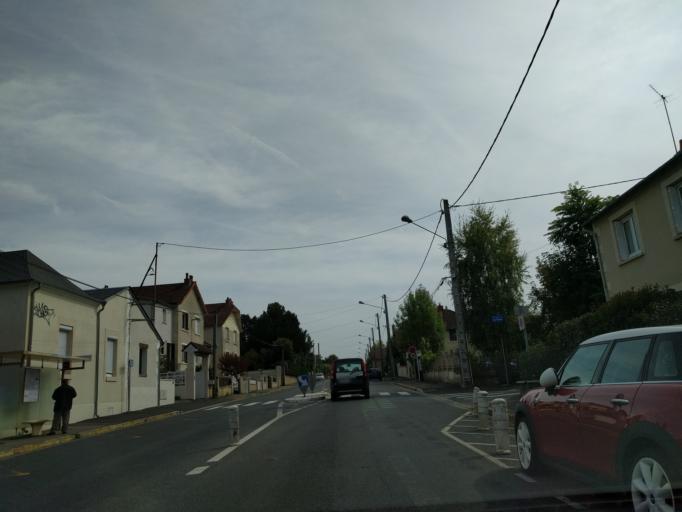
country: FR
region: Centre
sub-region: Departement du Cher
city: Bourges
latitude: 47.0642
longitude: 2.4205
